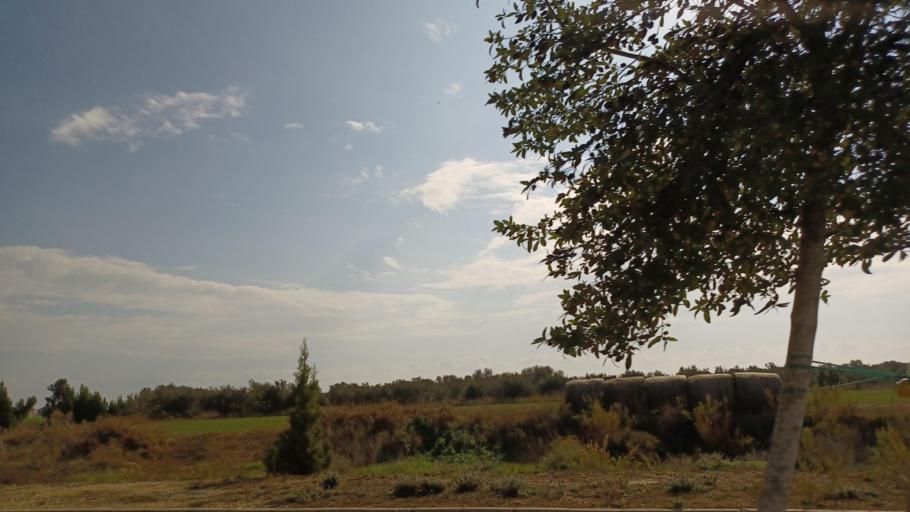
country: CY
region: Larnaka
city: Tersefanou
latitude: 34.8248
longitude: 33.5515
